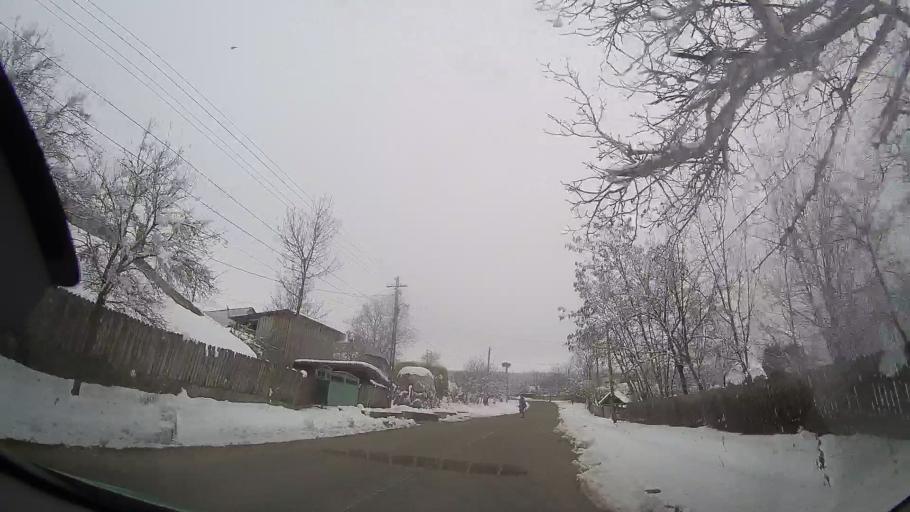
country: RO
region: Neamt
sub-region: Comuna Bozieni
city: Bozieni
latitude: 46.8506
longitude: 27.1791
